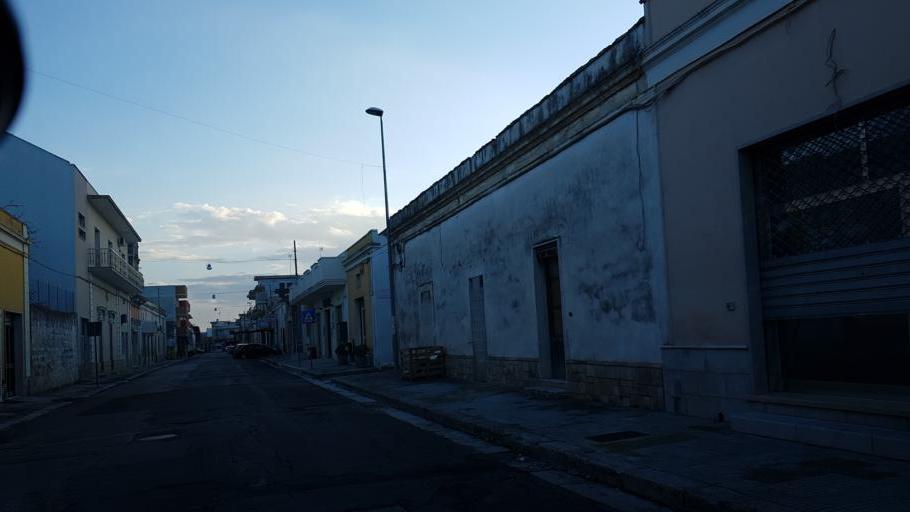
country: IT
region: Apulia
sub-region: Provincia di Lecce
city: Surbo
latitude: 40.3952
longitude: 18.1297
